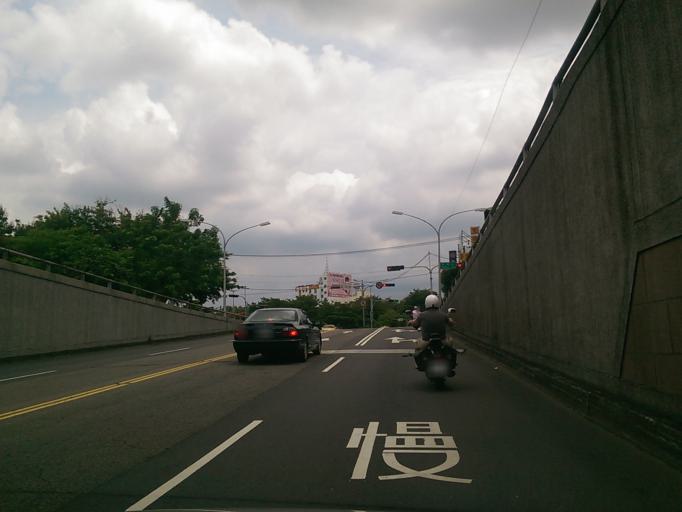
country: TW
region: Taiwan
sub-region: Taichung City
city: Taichung
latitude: 24.1410
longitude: 120.6957
